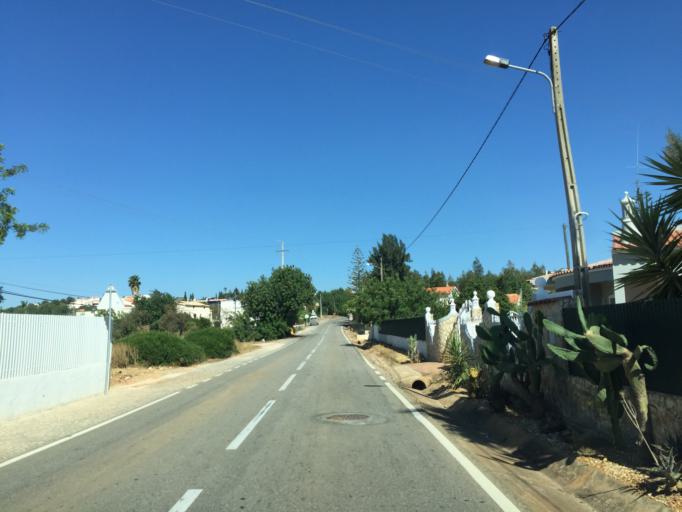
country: PT
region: Faro
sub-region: Loule
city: Vilamoura
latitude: 37.1128
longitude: -8.0900
